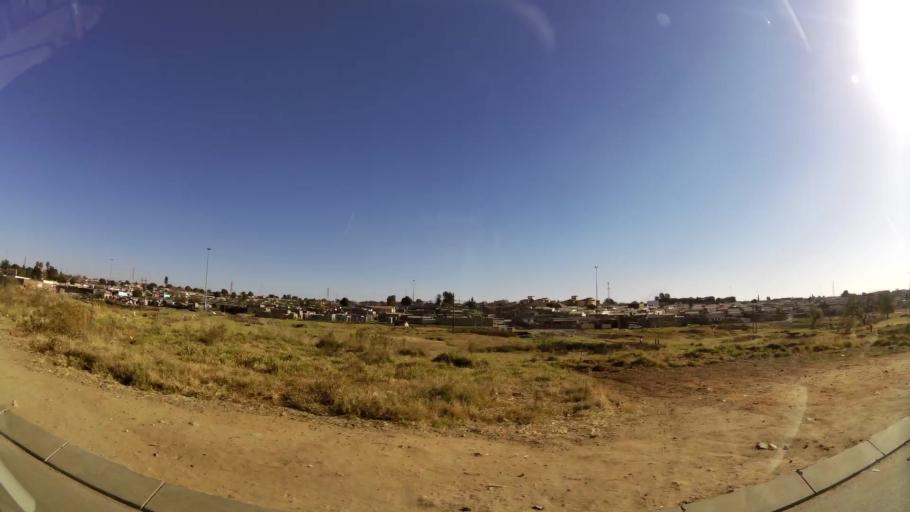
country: ZA
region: Gauteng
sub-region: Ekurhuleni Metropolitan Municipality
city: Tembisa
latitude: -26.0270
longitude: 28.2092
